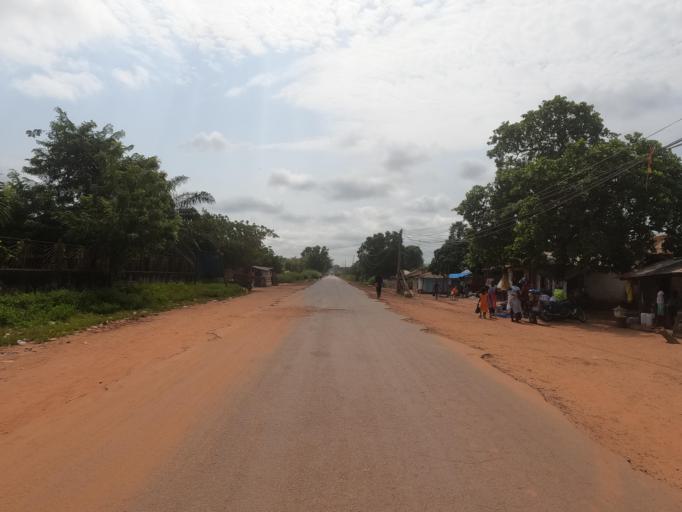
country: SN
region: Ziguinchor
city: Adeane
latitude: 12.4038
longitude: -15.7936
